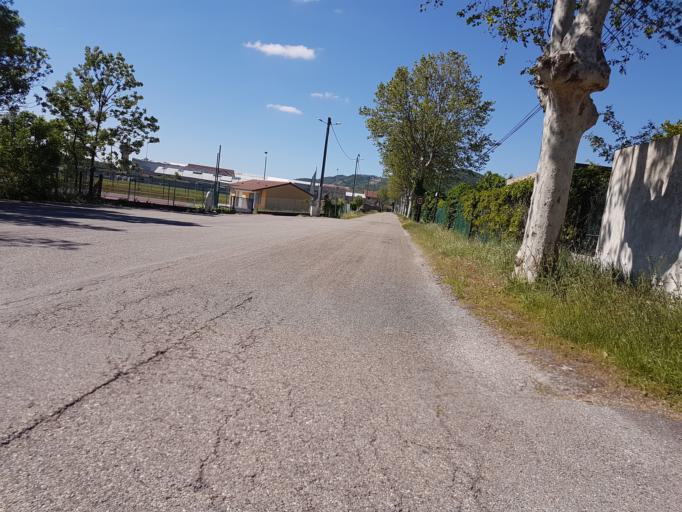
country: FR
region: Rhone-Alpes
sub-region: Departement de la Drome
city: Andancette
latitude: 45.2482
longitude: 4.8085
